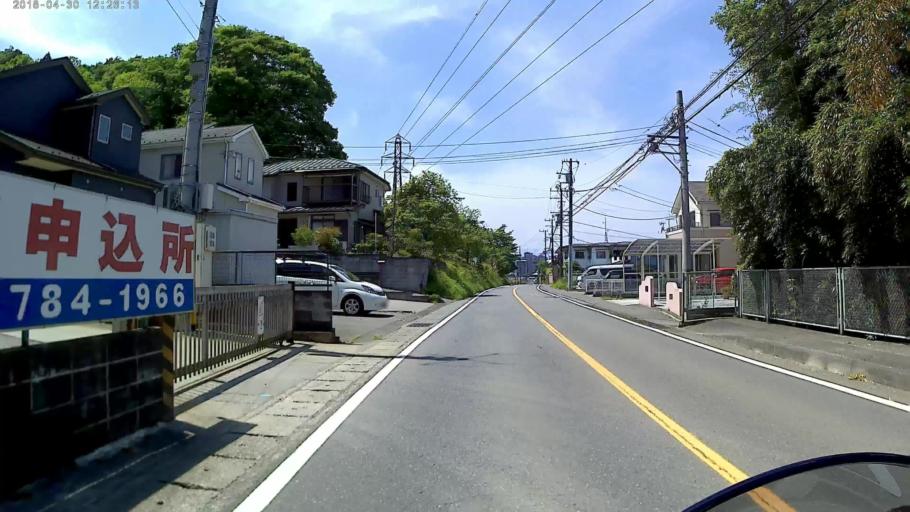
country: JP
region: Tokyo
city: Hachioji
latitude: 35.5820
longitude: 139.2680
